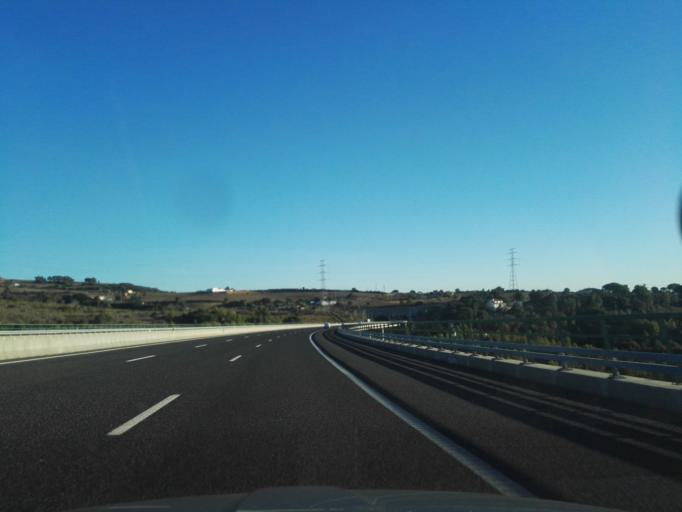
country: PT
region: Lisbon
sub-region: Arruda Dos Vinhos
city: Arruda dos Vinhos
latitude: 38.9364
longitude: -9.0727
